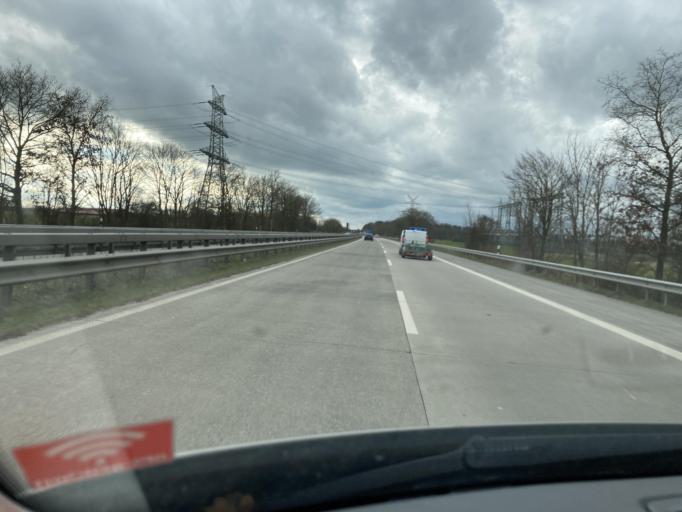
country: DE
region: Lower Saxony
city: Fedderwarden
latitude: 53.5553
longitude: 8.0673
